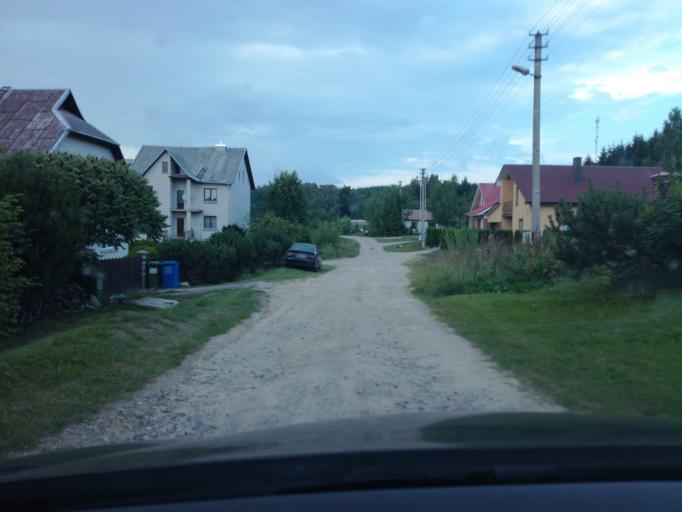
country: LT
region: Alytaus apskritis
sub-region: Alytus
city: Alytus
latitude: 54.3996
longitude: 24.0032
